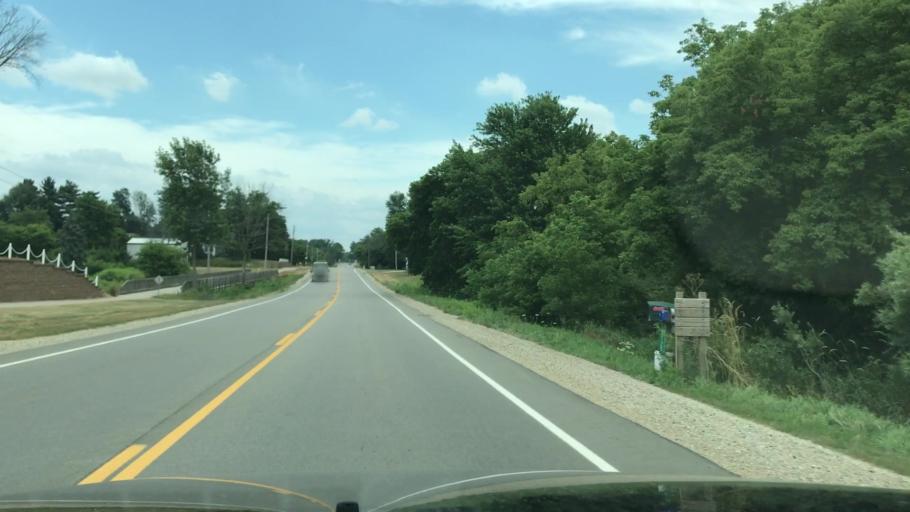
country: US
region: Michigan
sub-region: Ottawa County
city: Zeeland
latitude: 42.7831
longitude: -85.9584
